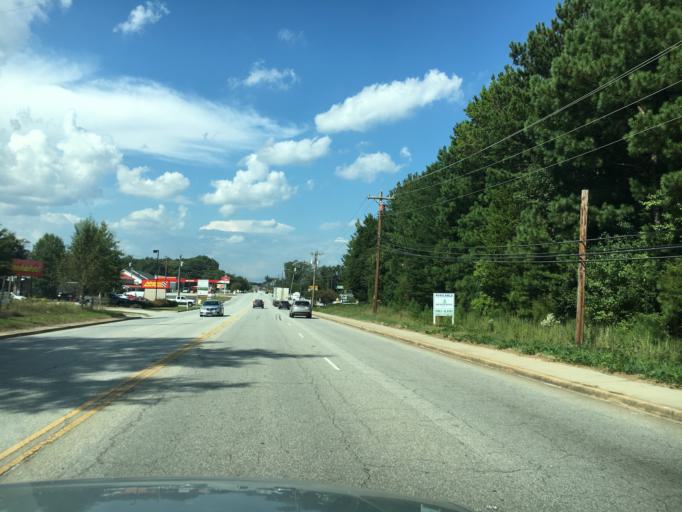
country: US
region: South Carolina
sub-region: Greenville County
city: Simpsonville
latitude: 34.7253
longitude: -82.2539
